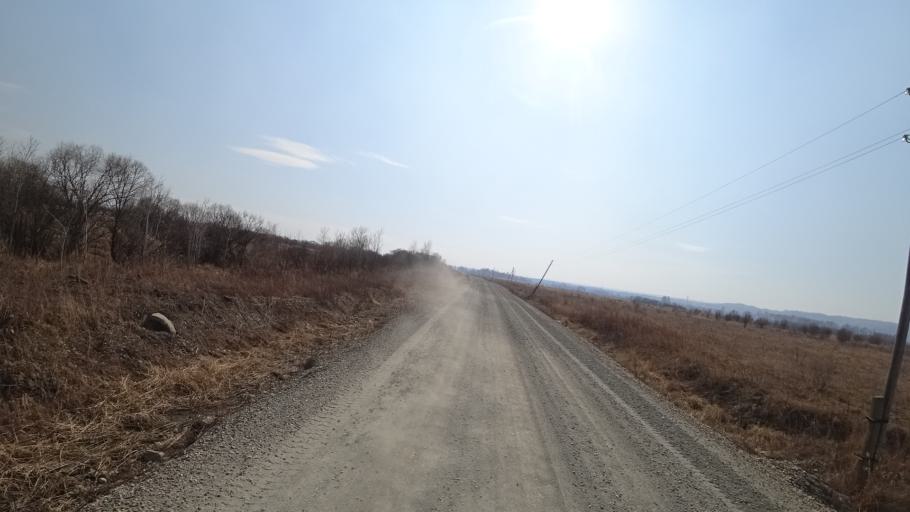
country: RU
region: Amur
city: Novobureyskiy
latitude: 49.8111
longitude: 129.9698
